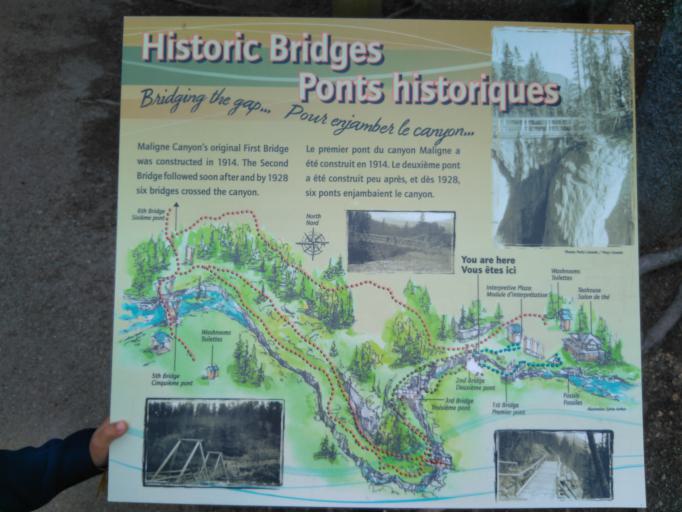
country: CA
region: Alberta
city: Jasper Park Lodge
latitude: 52.9201
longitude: -118.0028
